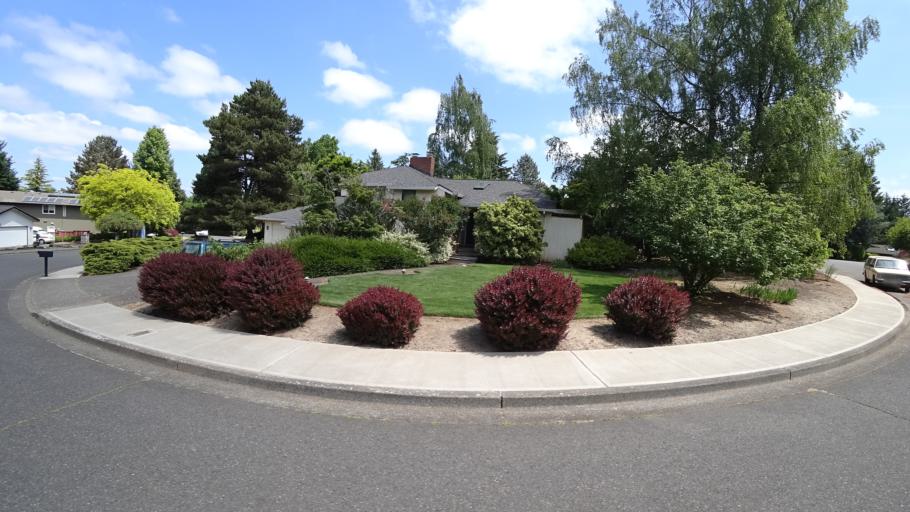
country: US
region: Oregon
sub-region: Clackamas County
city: Lake Oswego
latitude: 45.4378
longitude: -122.7045
